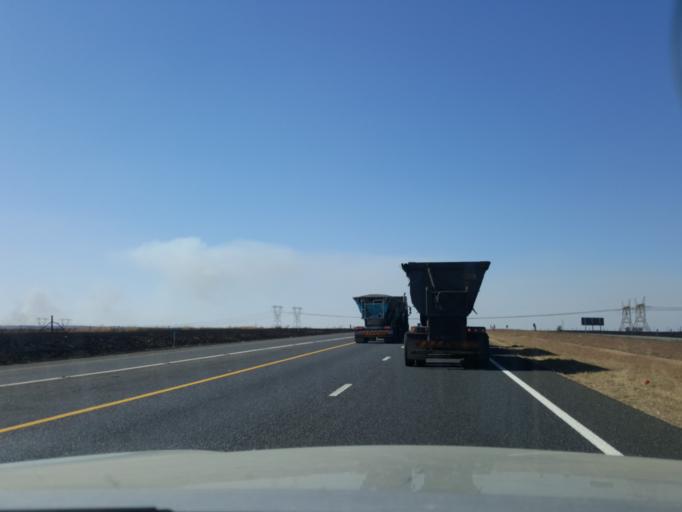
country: ZA
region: Mpumalanga
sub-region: Nkangala District Municipality
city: Delmas
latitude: -26.0231
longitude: 28.8866
